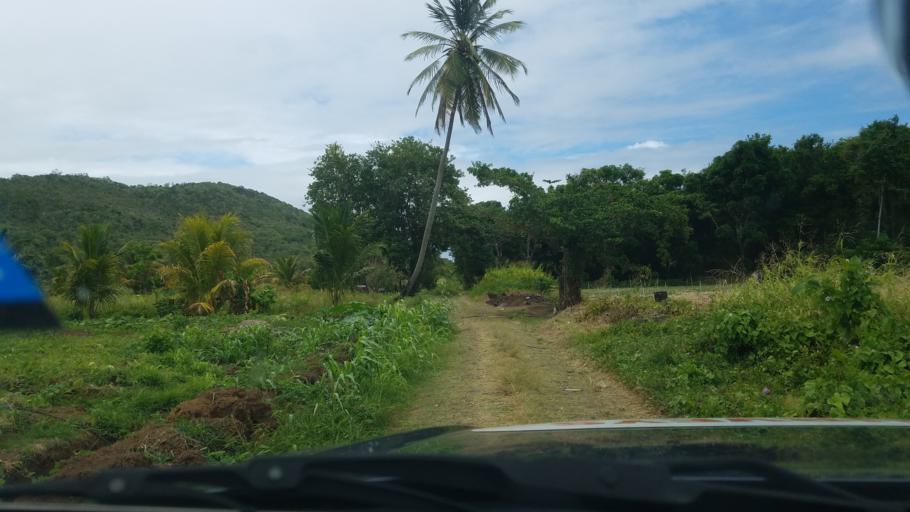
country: LC
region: Gros-Islet
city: Gros Islet
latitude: 14.0289
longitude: -60.9047
